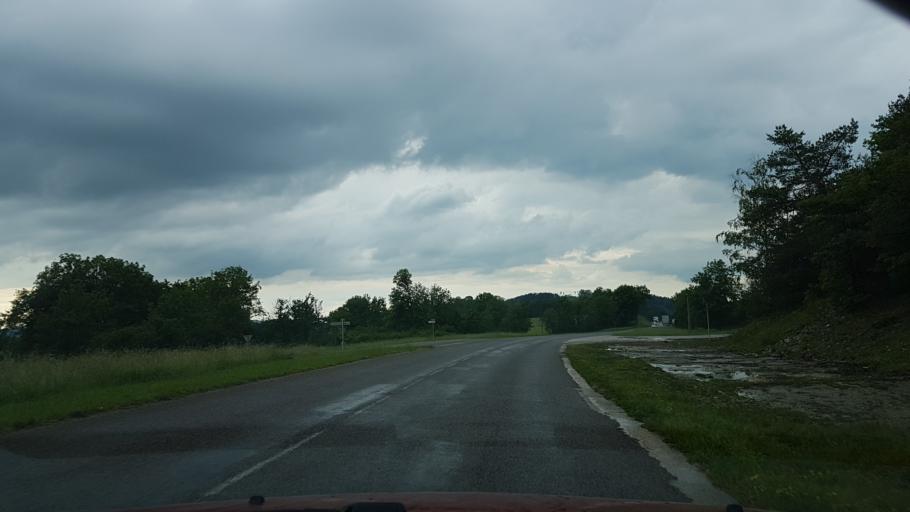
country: FR
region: Franche-Comte
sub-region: Departement du Jura
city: Clairvaux-les-Lacs
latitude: 46.5554
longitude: 5.7450
